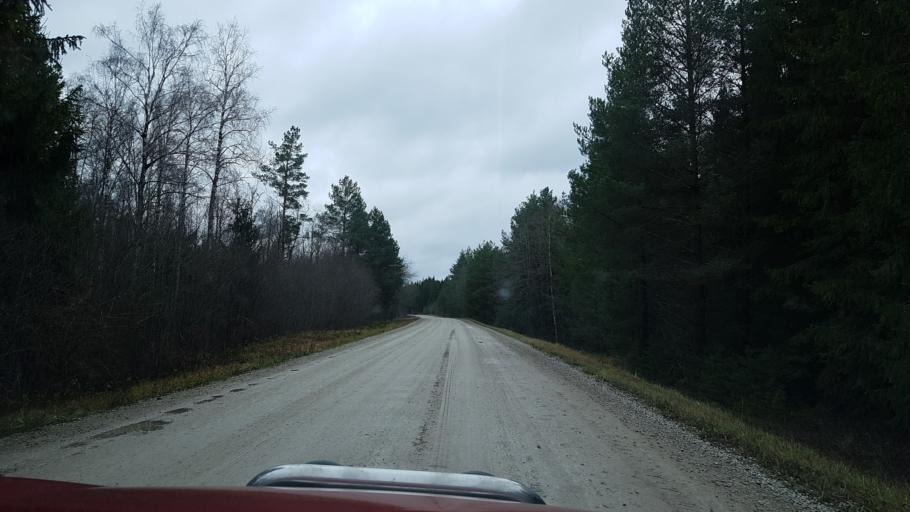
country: EE
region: Paernumaa
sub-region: Halinga vald
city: Parnu-Jaagupi
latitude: 58.5545
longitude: 24.4124
